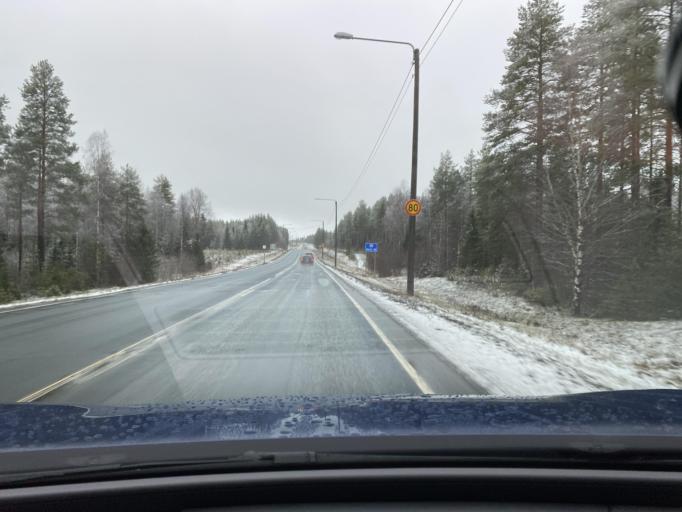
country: FI
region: Northern Ostrobothnia
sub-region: Oulu
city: Kiiminki
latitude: 65.1265
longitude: 25.7678
